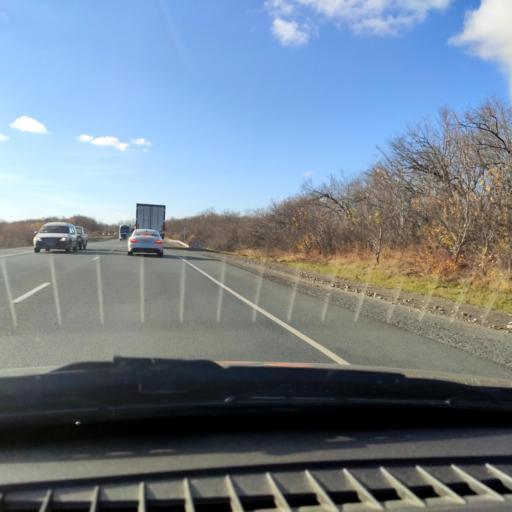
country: RU
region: Samara
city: Zhigulevsk
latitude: 53.3226
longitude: 49.3846
